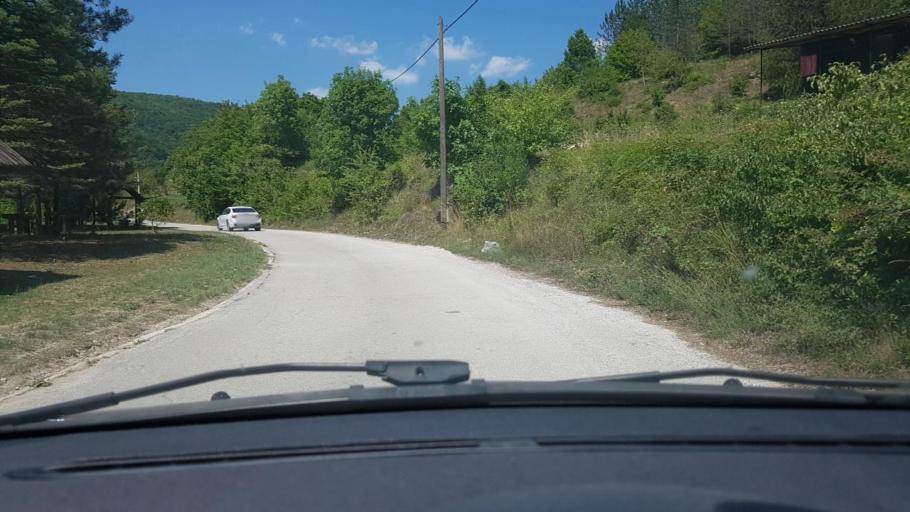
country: BA
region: Federation of Bosnia and Herzegovina
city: Orasac
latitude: 44.4938
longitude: 16.1424
